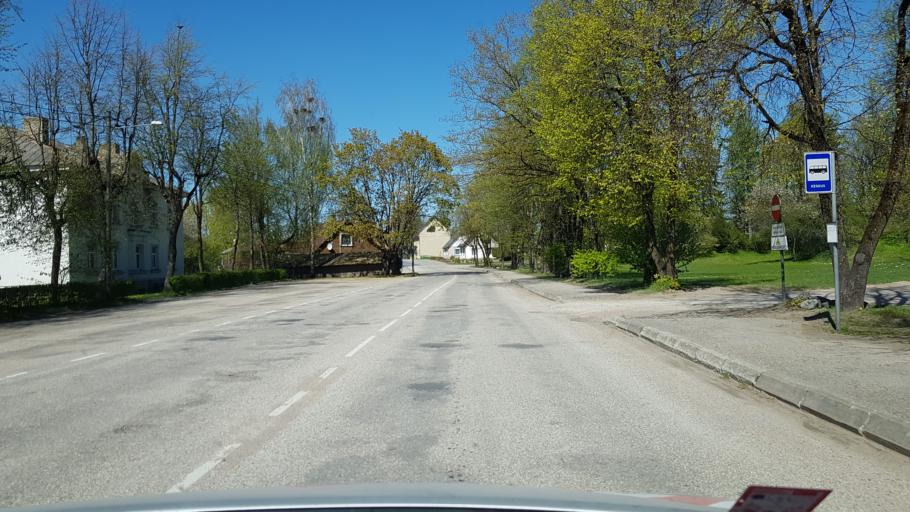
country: EE
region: Vorumaa
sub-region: Antsla vald
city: Vana-Antsla
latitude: 57.8293
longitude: 26.5284
